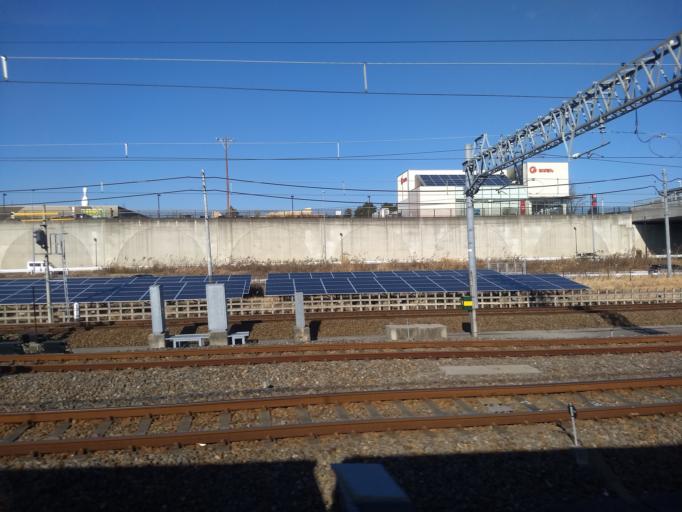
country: JP
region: Ibaraki
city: Ryugasaki
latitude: 35.8038
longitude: 140.1658
